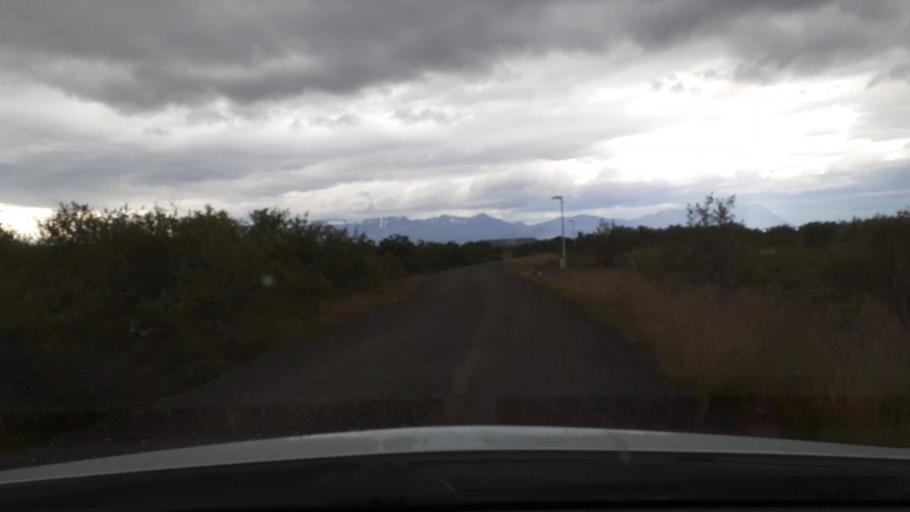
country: IS
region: West
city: Borgarnes
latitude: 64.6780
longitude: -21.7063
